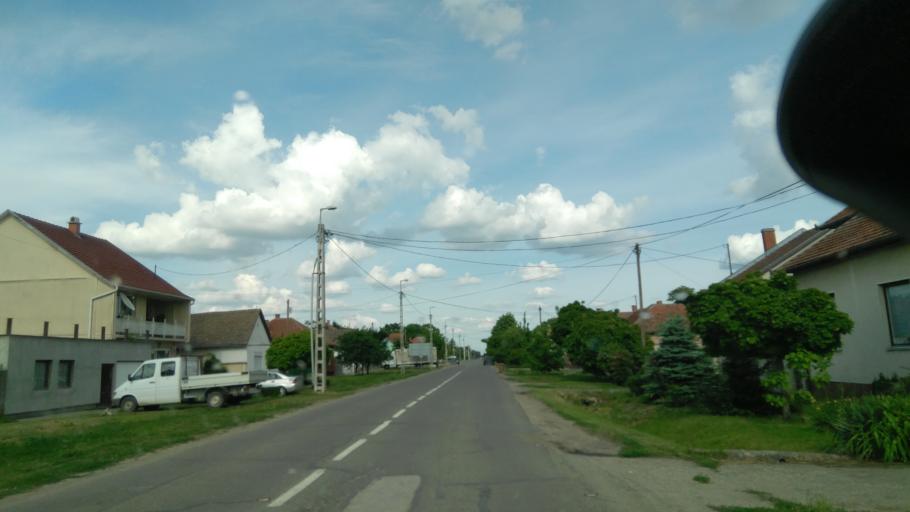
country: HU
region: Bekes
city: Battonya
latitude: 46.2922
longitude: 21.0174
